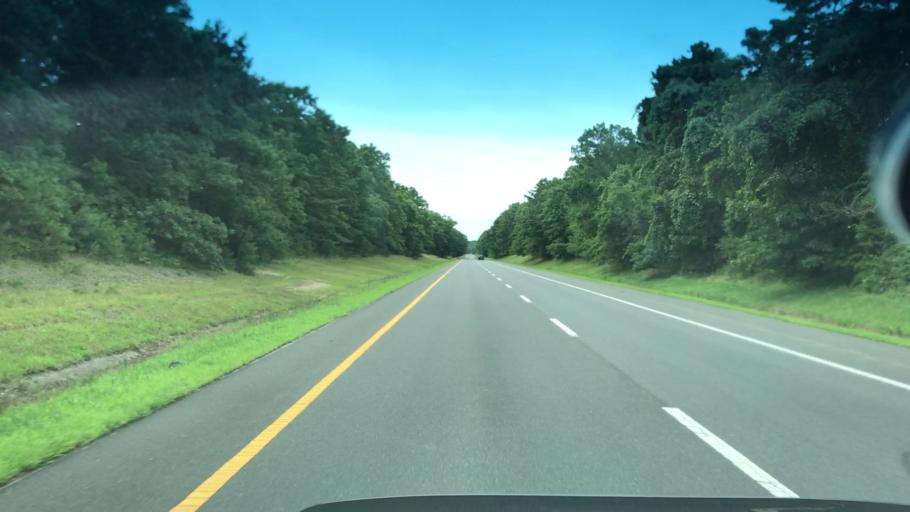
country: US
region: New York
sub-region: Suffolk County
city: East Shoreham
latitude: 40.9381
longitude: -72.8786
